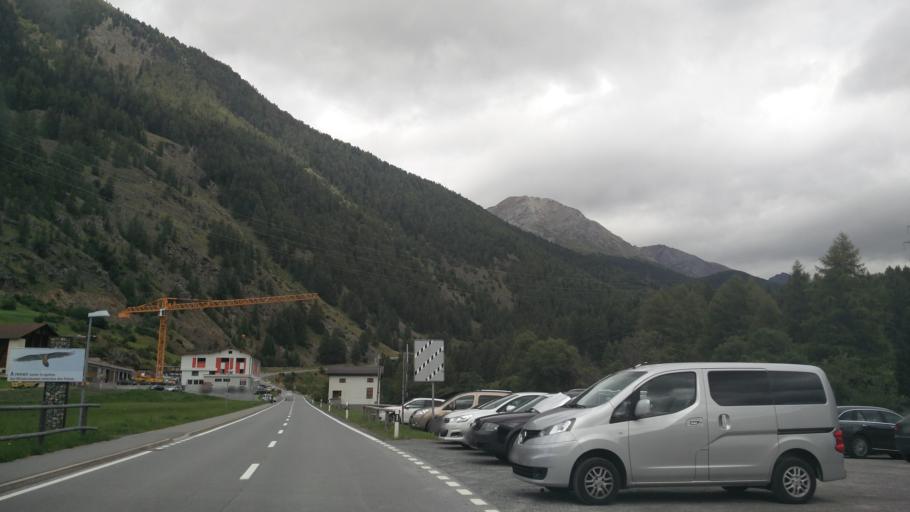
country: CH
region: Grisons
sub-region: Inn District
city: Zernez
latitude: 46.6961
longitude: 10.1015
